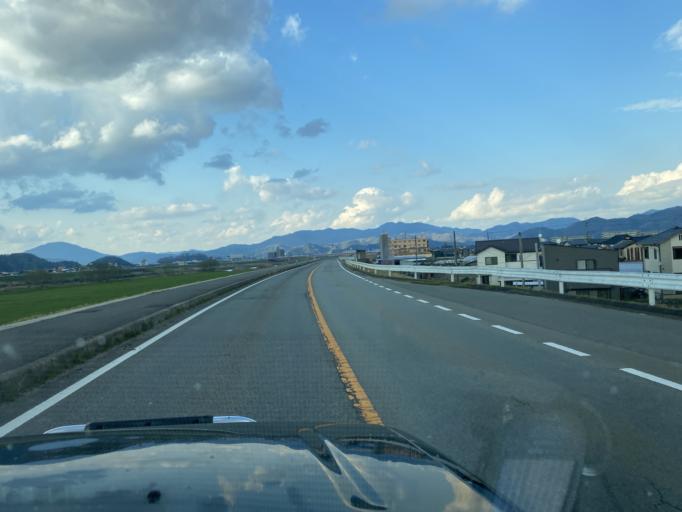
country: JP
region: Hyogo
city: Toyooka
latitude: 35.5175
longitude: 134.8242
